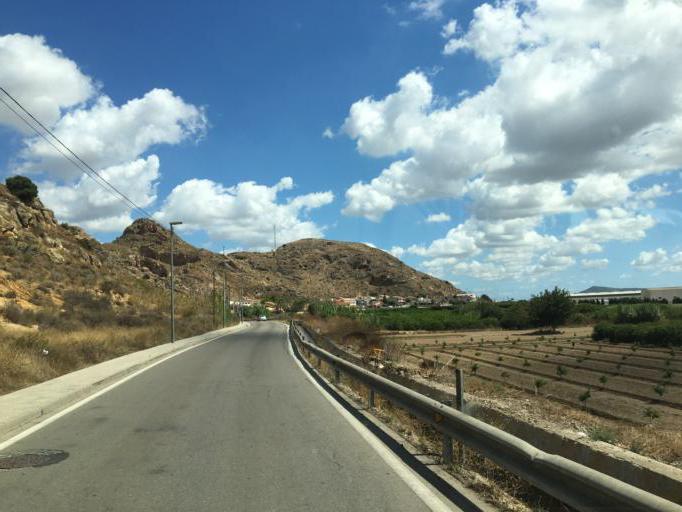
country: ES
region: Murcia
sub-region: Murcia
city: Santomera
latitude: 38.0511
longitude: -1.0661
